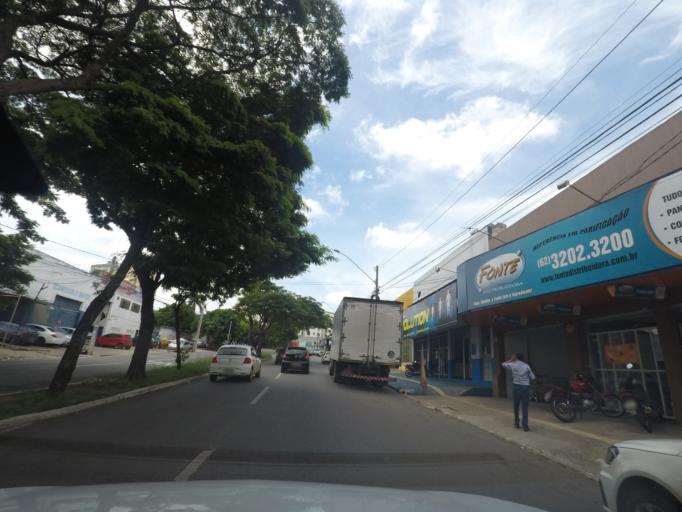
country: BR
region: Goias
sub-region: Goiania
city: Goiania
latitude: -16.6684
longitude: -49.2367
